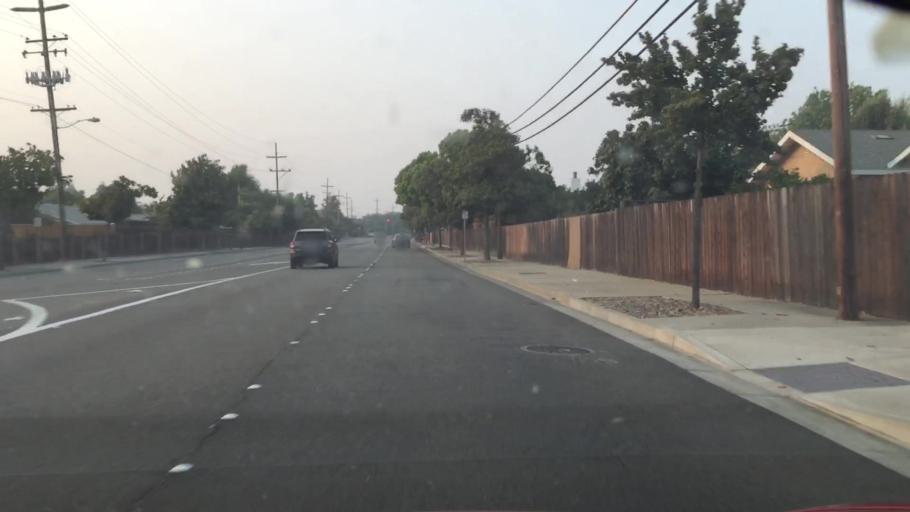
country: US
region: California
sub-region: Alameda County
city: Livermore
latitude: 37.6696
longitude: -121.7803
